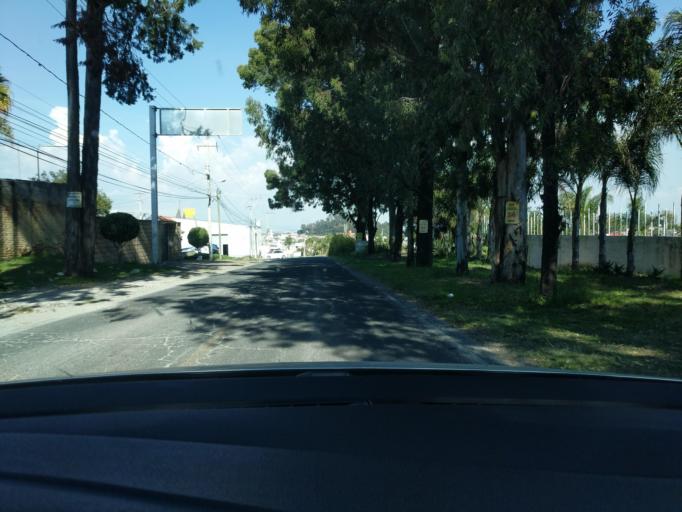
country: MX
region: Puebla
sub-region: Ocoyucan
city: San Bernabe Temoxtitla
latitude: 19.0015
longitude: -98.3411
